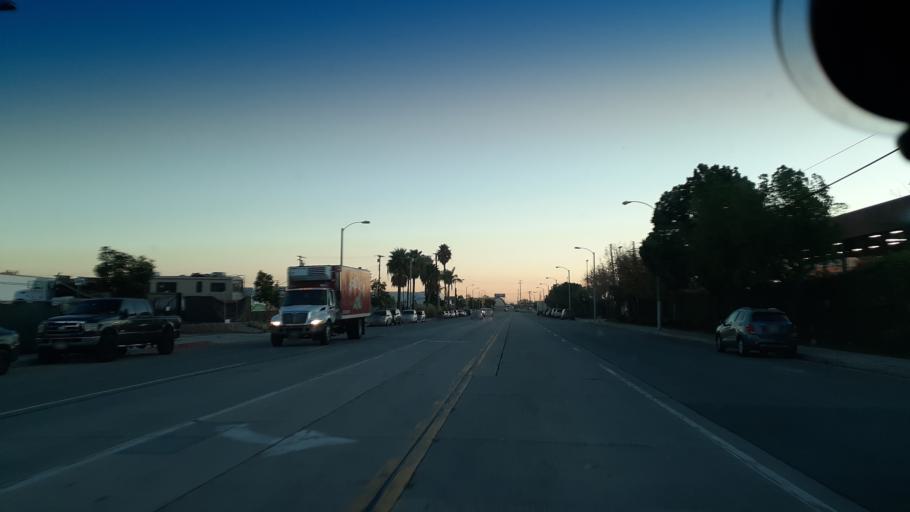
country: US
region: California
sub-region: Los Angeles County
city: Carson
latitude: 33.8599
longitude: -118.2786
